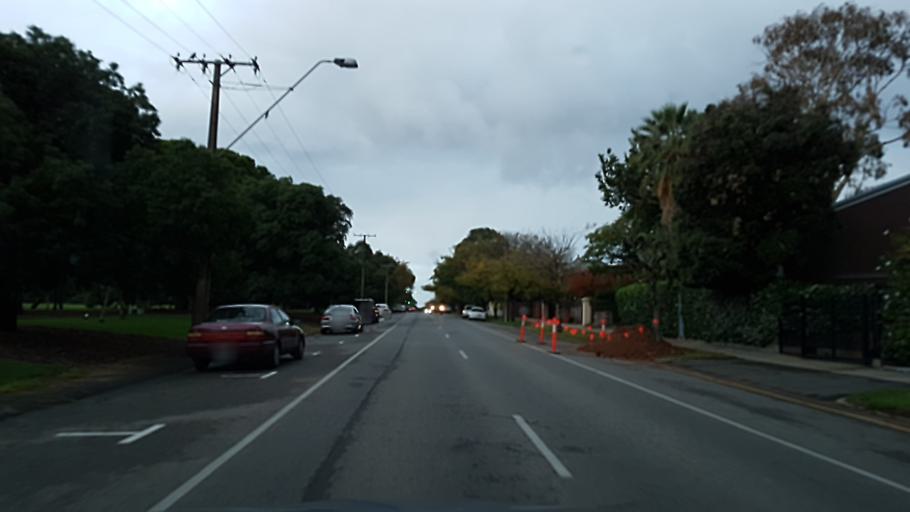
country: AU
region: South Australia
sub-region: Adelaide
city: North Adelaide
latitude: -34.9035
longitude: 138.5873
